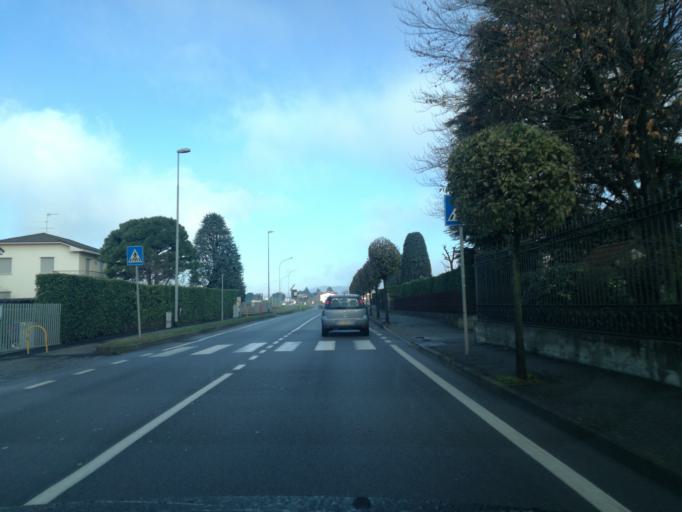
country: IT
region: Lombardy
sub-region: Provincia di Lecco
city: Verderio Inferiore
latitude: 45.6713
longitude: 9.4345
